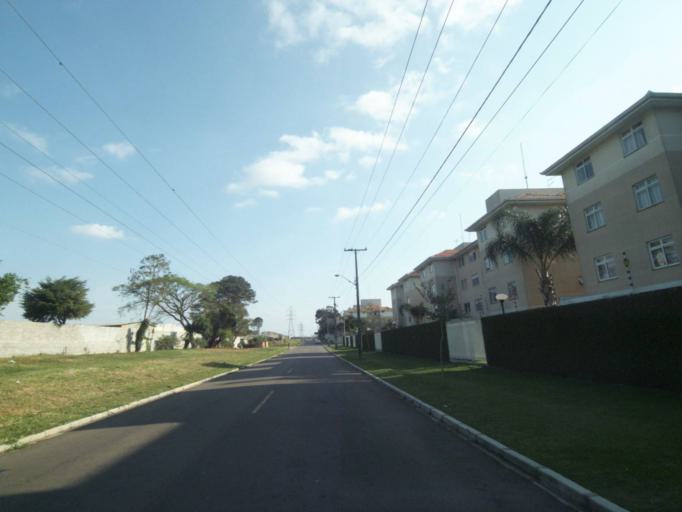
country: BR
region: Parana
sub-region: Curitiba
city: Curitiba
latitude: -25.4857
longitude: -49.3223
